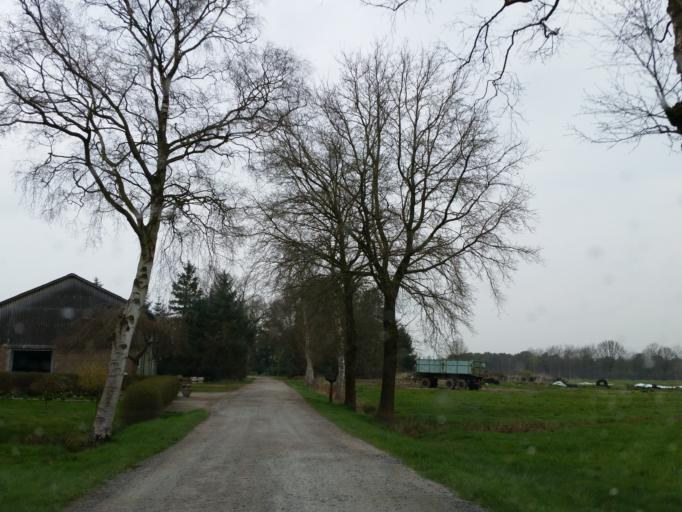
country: DE
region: Lower Saxony
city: Armstorf
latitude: 53.5818
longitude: 9.0110
